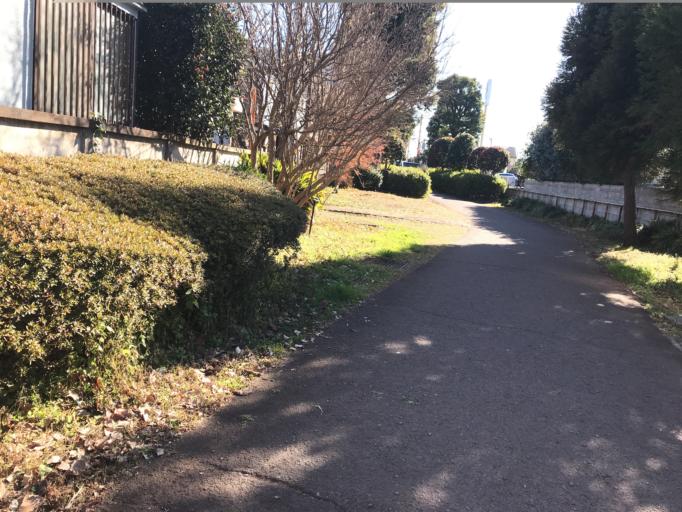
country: JP
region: Tokyo
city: Hino
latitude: 35.7104
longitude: 139.4259
